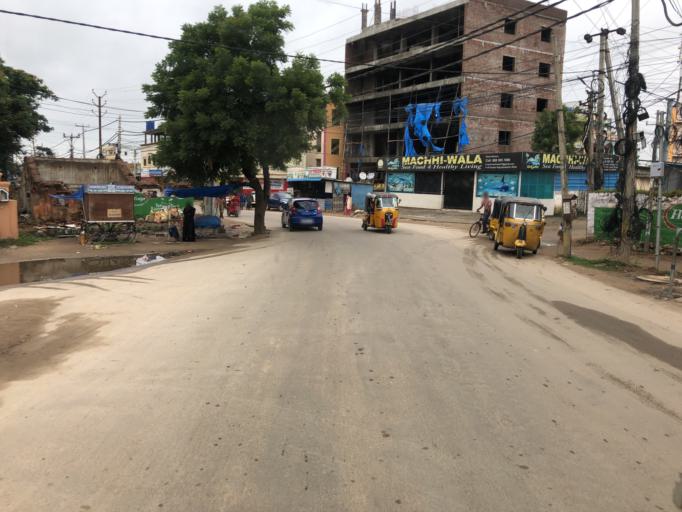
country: IN
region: Telangana
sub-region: Medak
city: Serilingampalle
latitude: 17.4652
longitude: 78.3438
